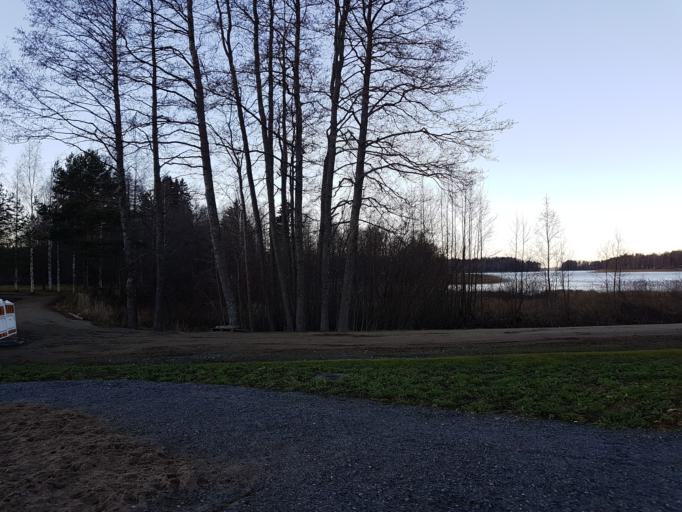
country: FI
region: Northern Savo
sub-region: Kuopio
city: Kuopio
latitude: 62.9283
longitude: 27.6293
